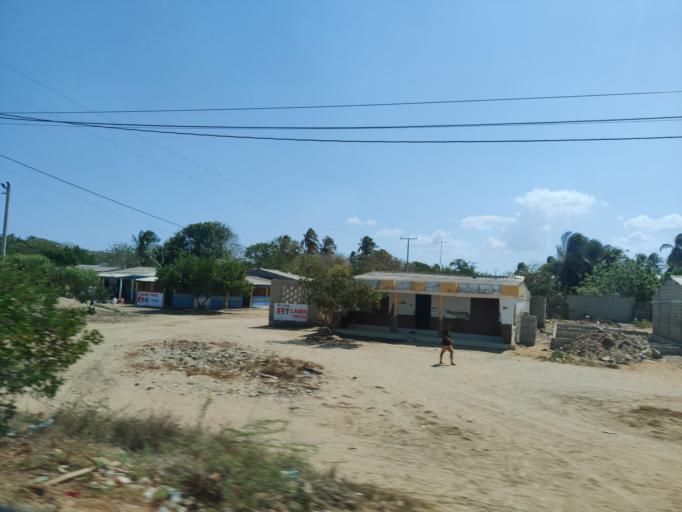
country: CO
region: Bolivar
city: Santa Catalina
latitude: 10.7388
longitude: -75.2633
